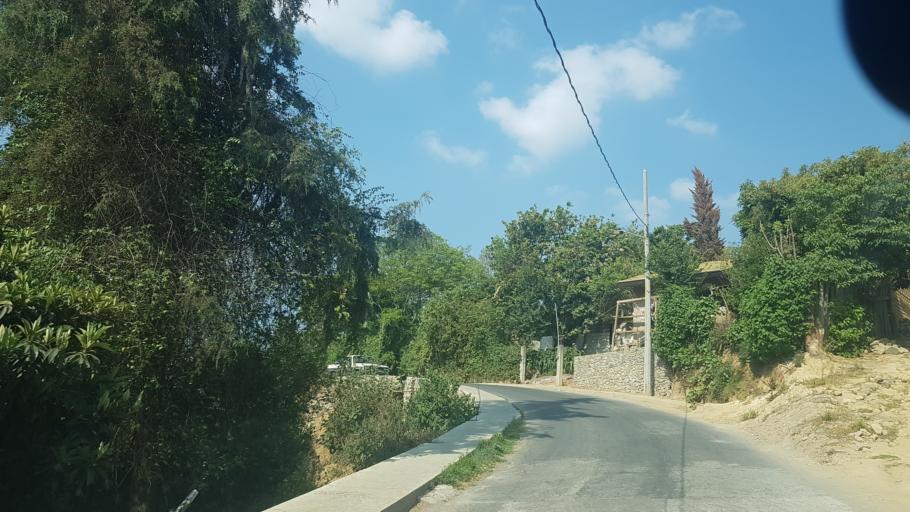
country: MX
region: Morelos
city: Hueyapan
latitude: 18.8880
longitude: -98.6864
